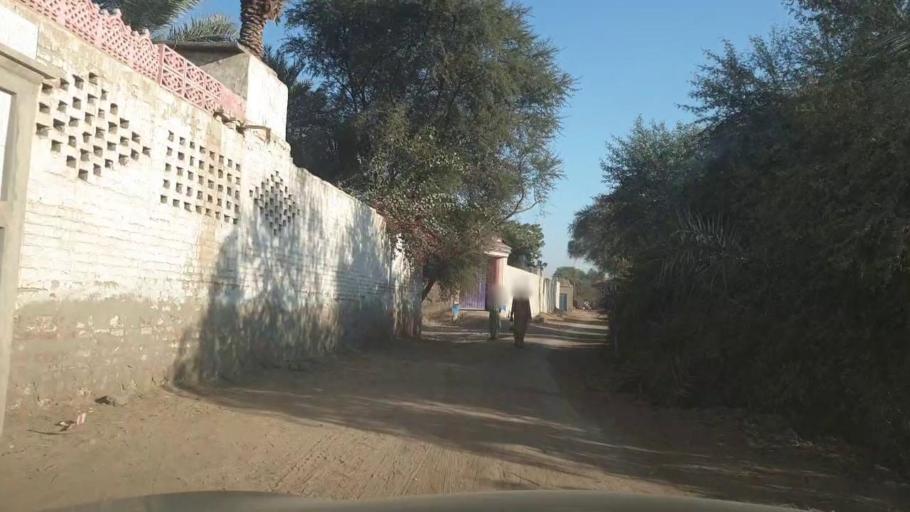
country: PK
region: Sindh
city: Ghotki
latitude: 28.0675
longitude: 69.3684
